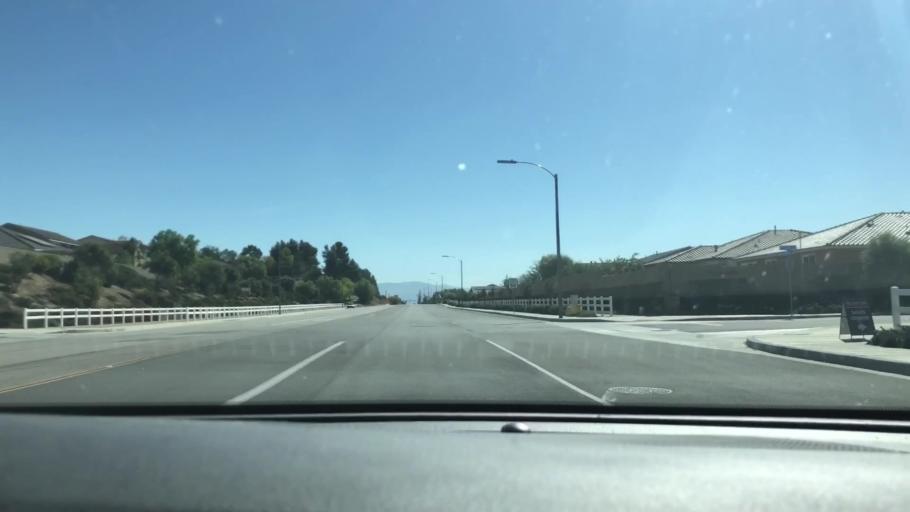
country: US
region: California
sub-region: Riverside County
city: Wildomar
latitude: 33.5942
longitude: -117.2591
